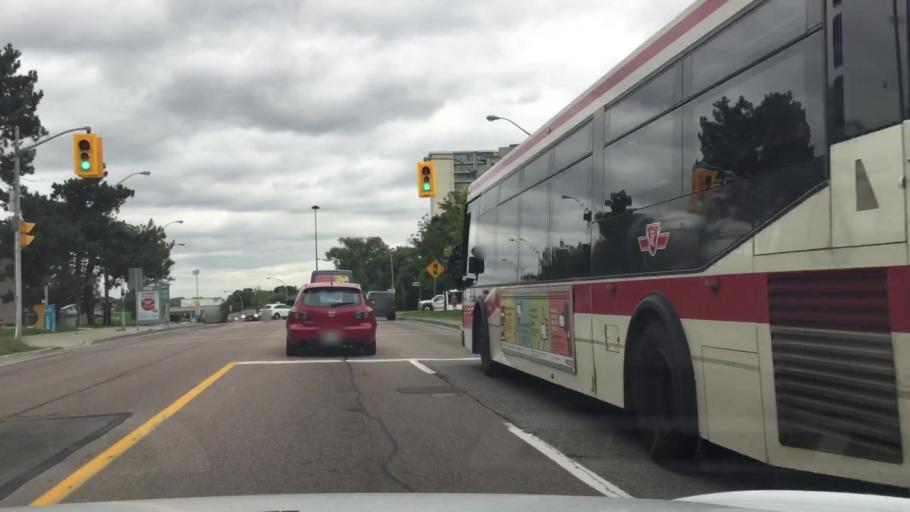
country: CA
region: Ontario
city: Willowdale
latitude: 43.7598
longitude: -79.3317
